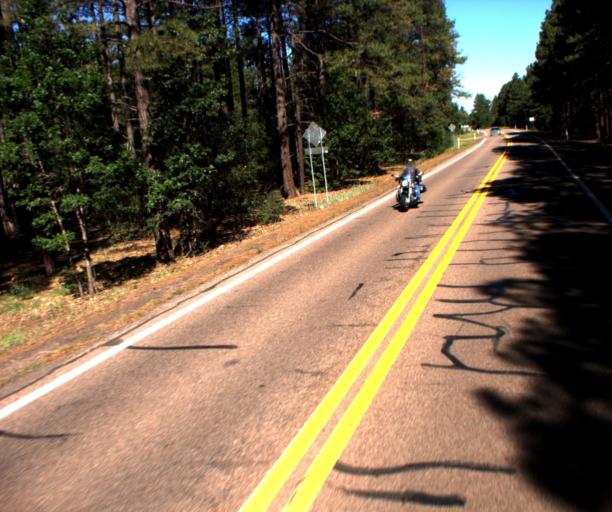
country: US
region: Arizona
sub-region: Navajo County
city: Pinetop-Lakeside
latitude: 34.0755
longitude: -109.8637
